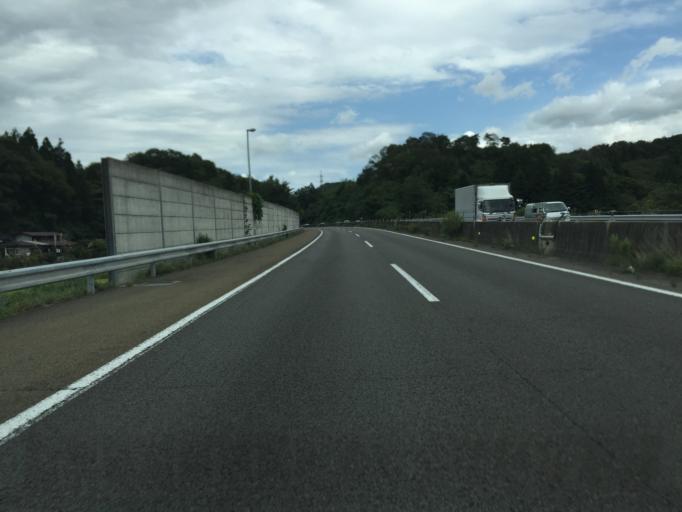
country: JP
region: Miyagi
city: Sendai
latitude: 38.1861
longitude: 140.7712
